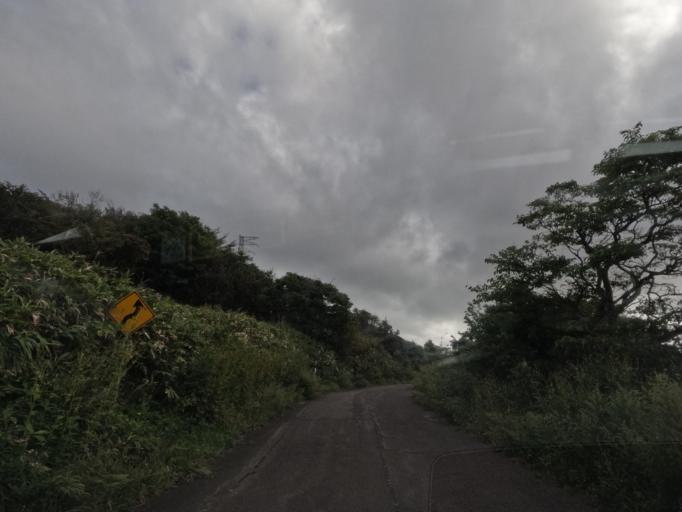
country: JP
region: Hokkaido
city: Muroran
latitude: 42.3293
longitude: 141.0021
